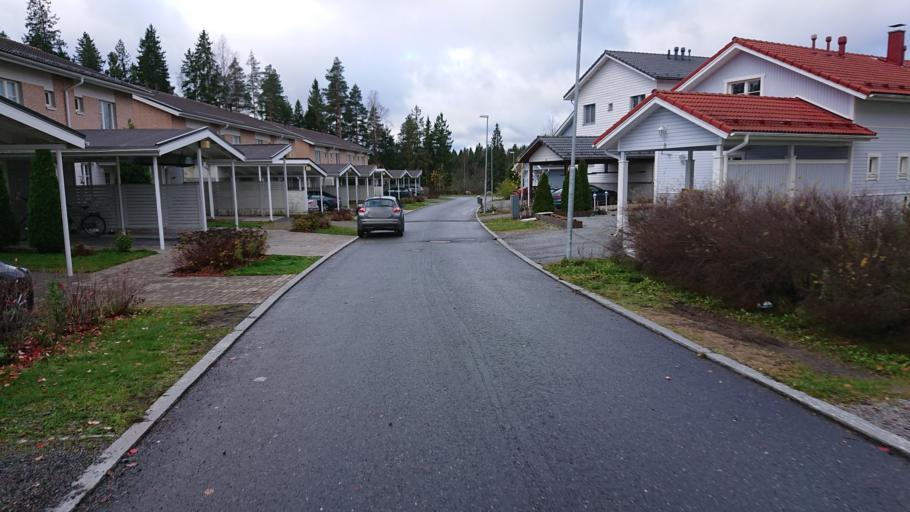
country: FI
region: Pirkanmaa
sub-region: Tampere
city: Tampere
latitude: 61.4374
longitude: 23.8434
